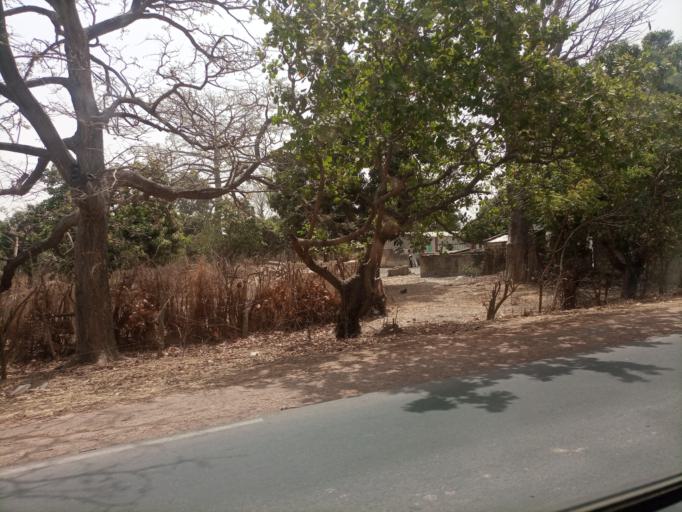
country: SN
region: Fatick
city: Sokone
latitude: 13.7063
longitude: -16.4289
